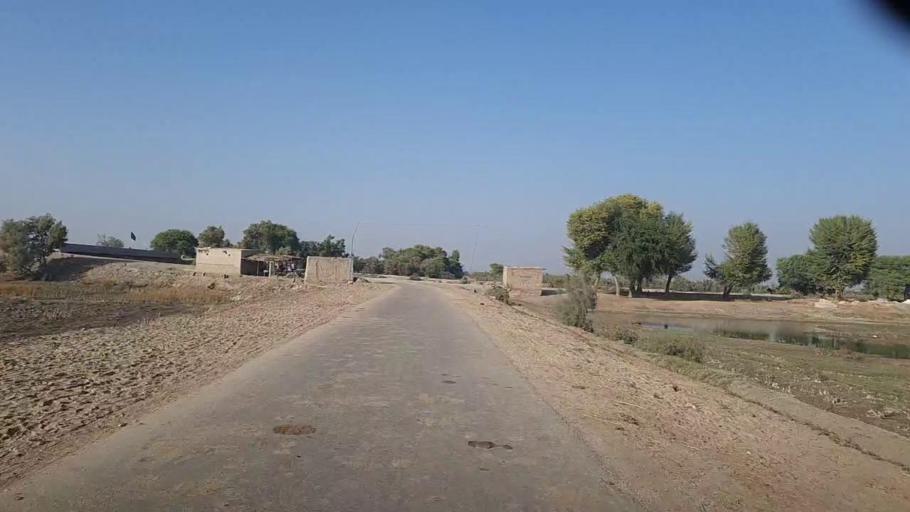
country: PK
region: Sindh
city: Tangwani
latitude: 28.2997
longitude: 68.9519
